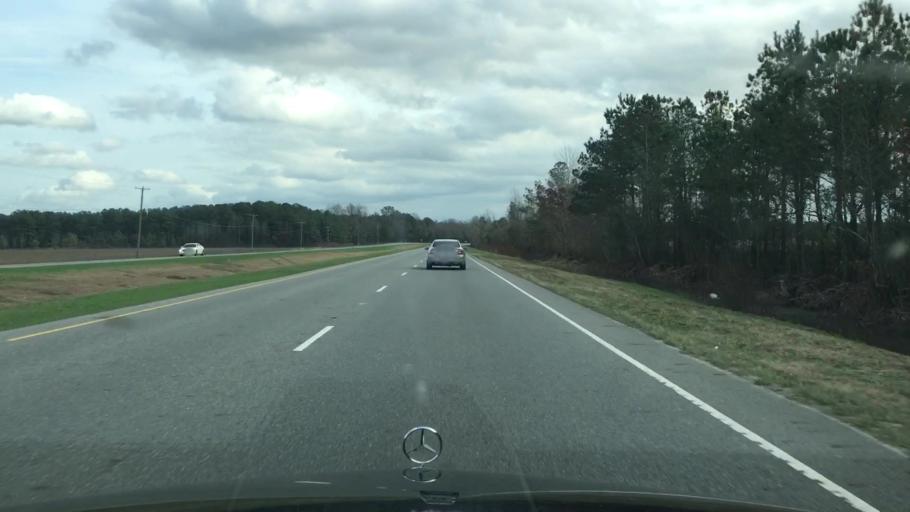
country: US
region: North Carolina
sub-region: Duplin County
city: Kenansville
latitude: 34.9486
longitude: -77.8843
